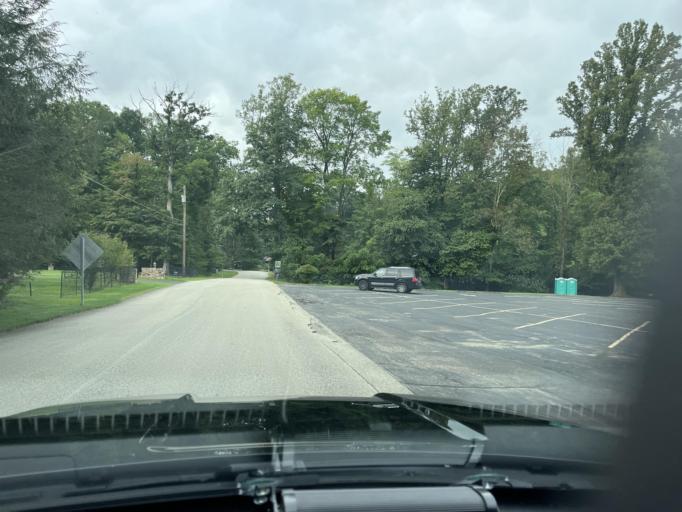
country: US
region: Pennsylvania
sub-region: Fayette County
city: Hopwood
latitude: 39.8622
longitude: -79.7015
